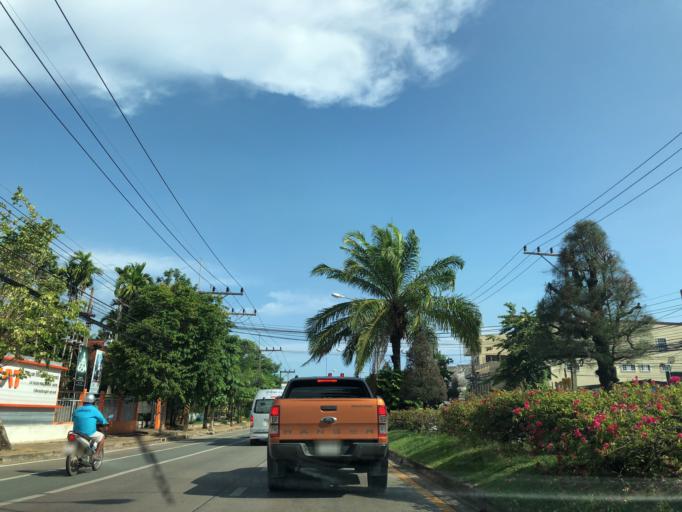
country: TH
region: Krabi
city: Krabi
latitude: 8.0815
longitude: 98.9149
